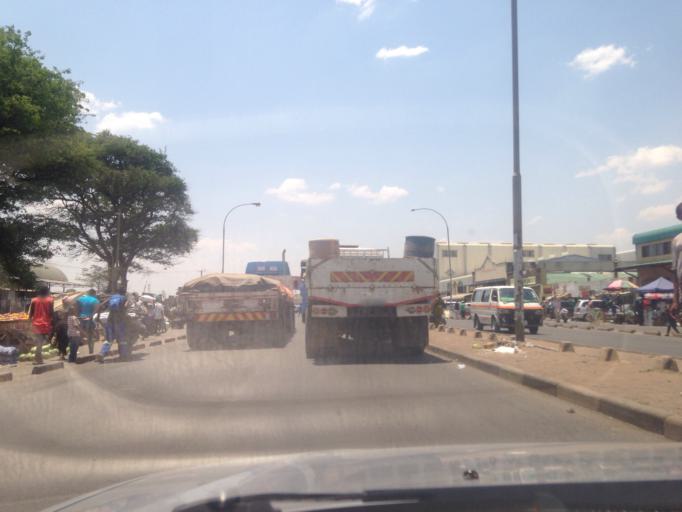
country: ZM
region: Lusaka
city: Lusaka
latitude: -15.4149
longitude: 28.2772
